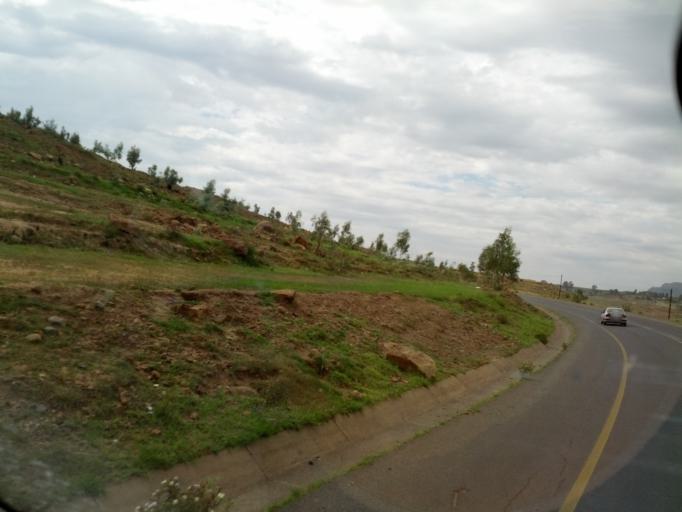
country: LS
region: Maseru
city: Maseru
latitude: -29.3911
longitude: 27.5041
